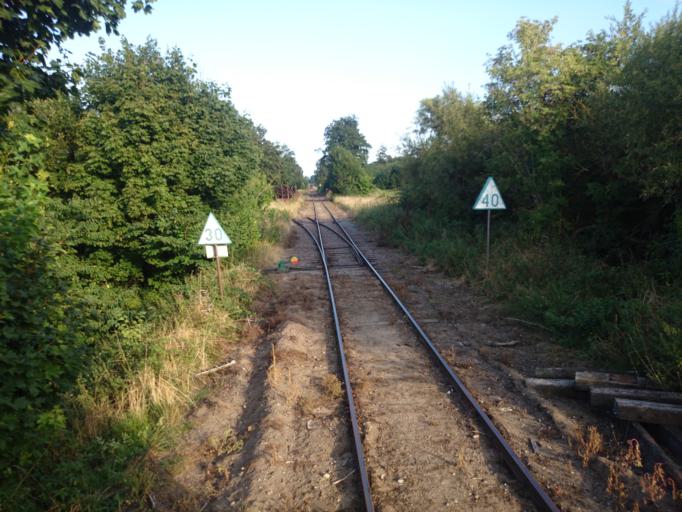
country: SE
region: Skane
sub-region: Simrishamns Kommun
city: Kivik
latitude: 55.7100
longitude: 14.1473
